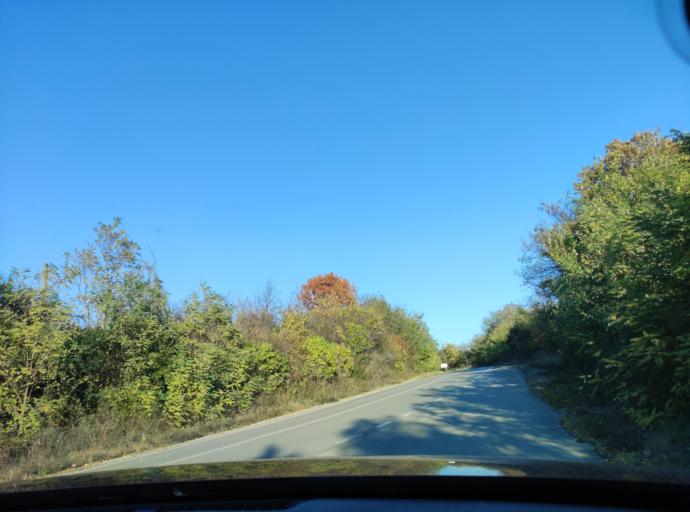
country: BG
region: Montana
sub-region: Obshtina Chiprovtsi
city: Chiprovtsi
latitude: 43.4328
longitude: 22.9626
